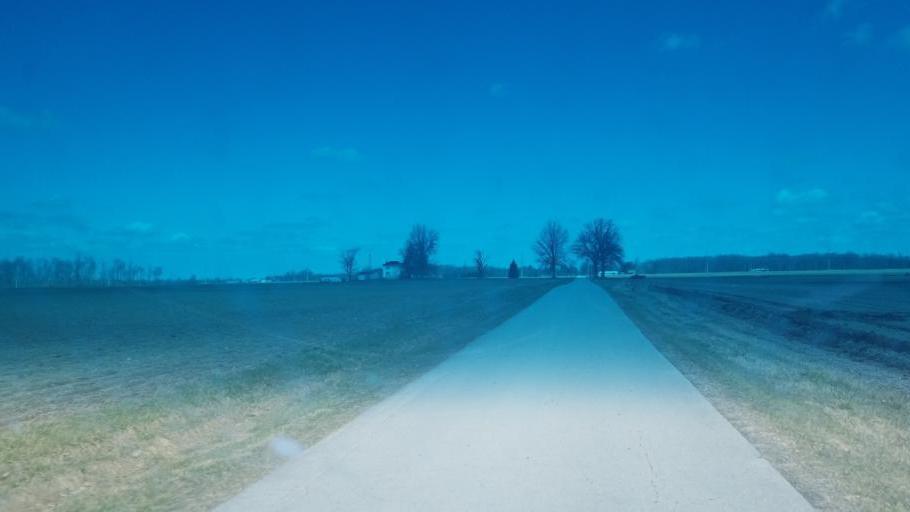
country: US
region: Ohio
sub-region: Crawford County
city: Bucyrus
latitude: 40.8297
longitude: -83.0738
